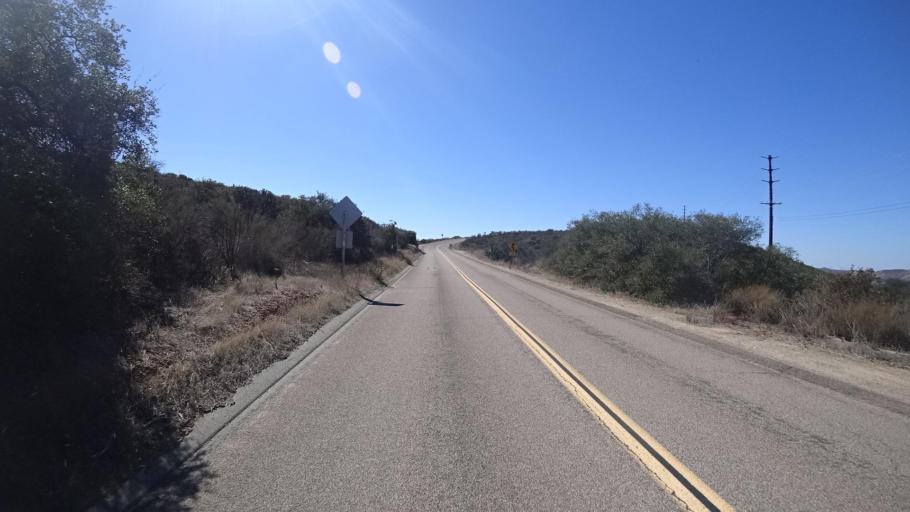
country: US
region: California
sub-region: San Diego County
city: Alpine
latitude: 32.7981
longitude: -116.7710
